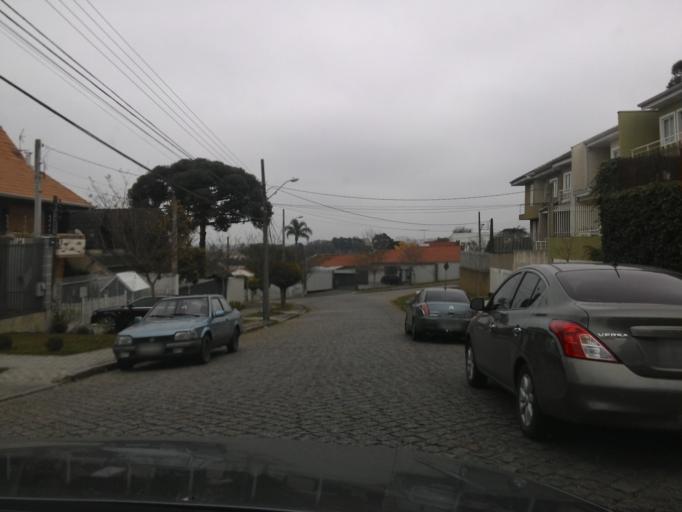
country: BR
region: Parana
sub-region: Curitiba
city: Curitiba
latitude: -25.4600
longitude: -49.2434
